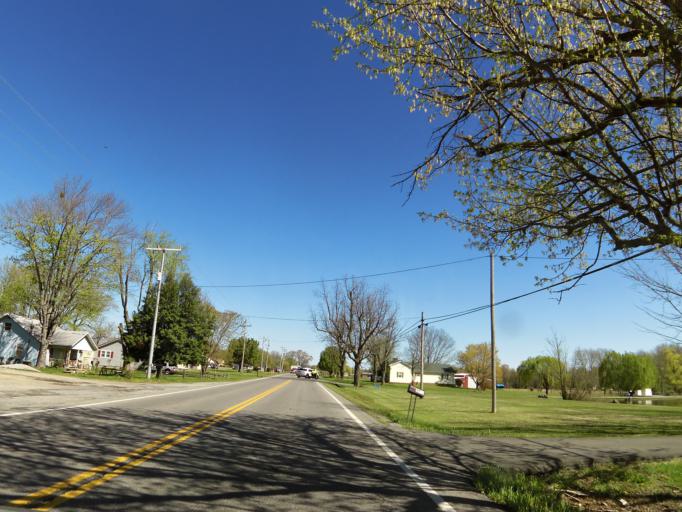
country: US
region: Tennessee
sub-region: Robertson County
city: Springfield
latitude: 36.5508
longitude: -86.8642
